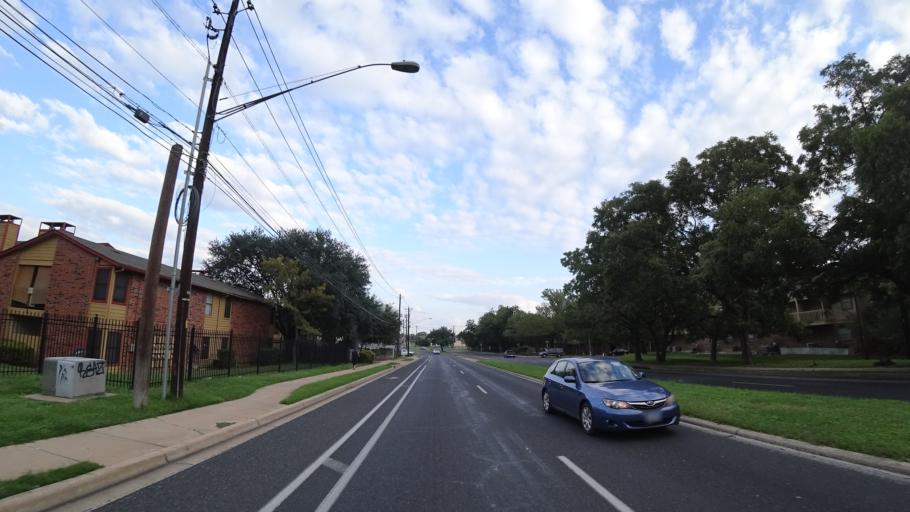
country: US
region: Texas
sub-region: Travis County
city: Rollingwood
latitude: 30.2098
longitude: -97.7853
